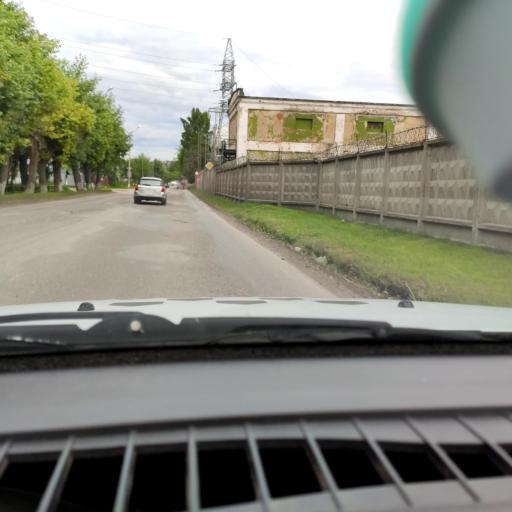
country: RU
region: Perm
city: Chusovoy
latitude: 58.2934
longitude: 57.8151
